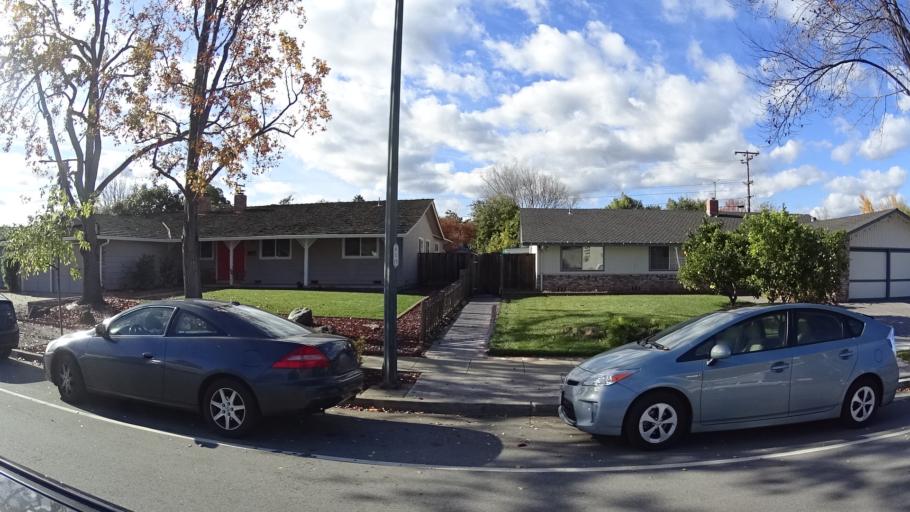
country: US
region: California
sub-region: Santa Clara County
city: Cupertino
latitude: 37.3435
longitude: -122.0451
